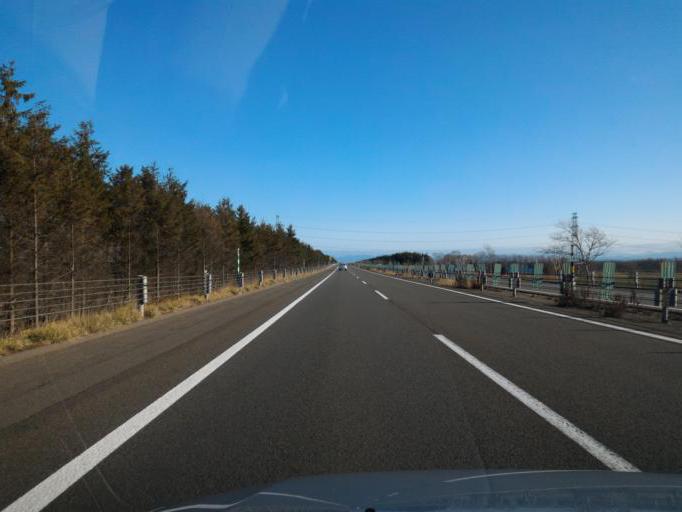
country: JP
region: Hokkaido
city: Ebetsu
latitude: 43.1173
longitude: 141.6237
